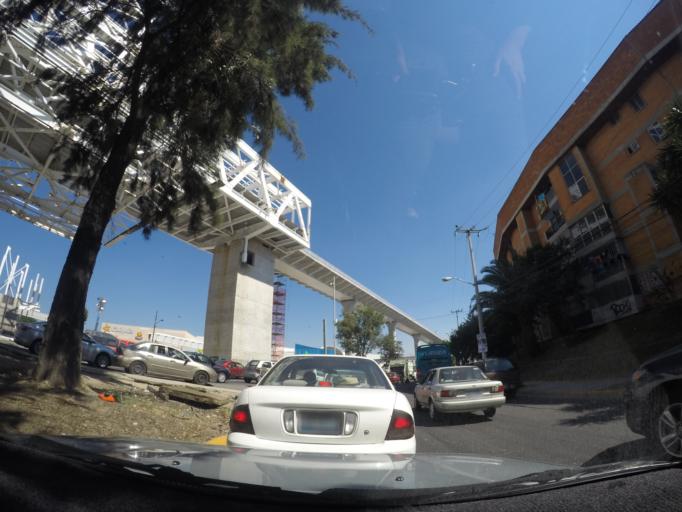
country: MX
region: Jalisco
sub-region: Zapotlanejo
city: La Mezquitera
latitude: 20.5661
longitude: -103.0777
